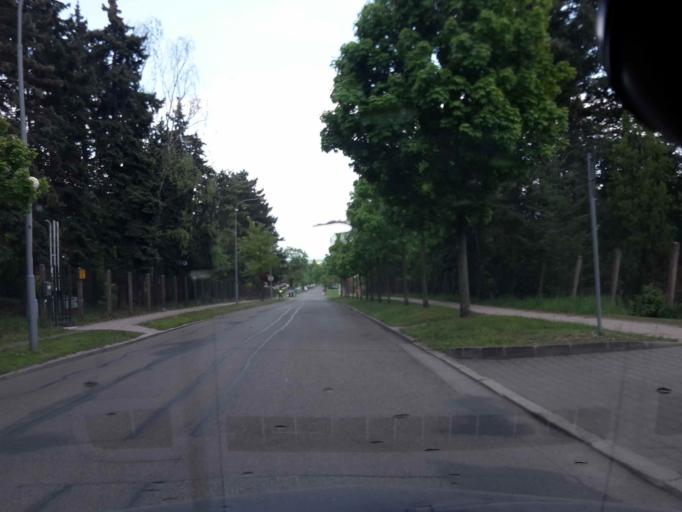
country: CZ
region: South Moravian
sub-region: Mesto Brno
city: Brno
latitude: 49.2249
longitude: 16.6322
